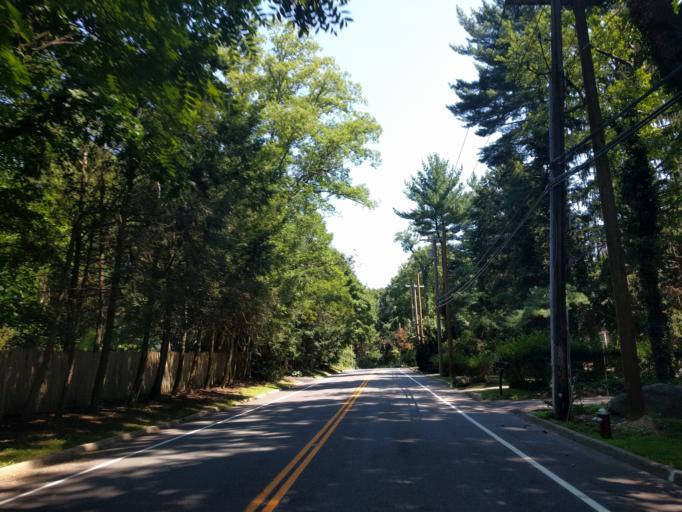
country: US
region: New York
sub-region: Nassau County
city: Lattingtown
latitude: 40.8882
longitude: -73.6014
